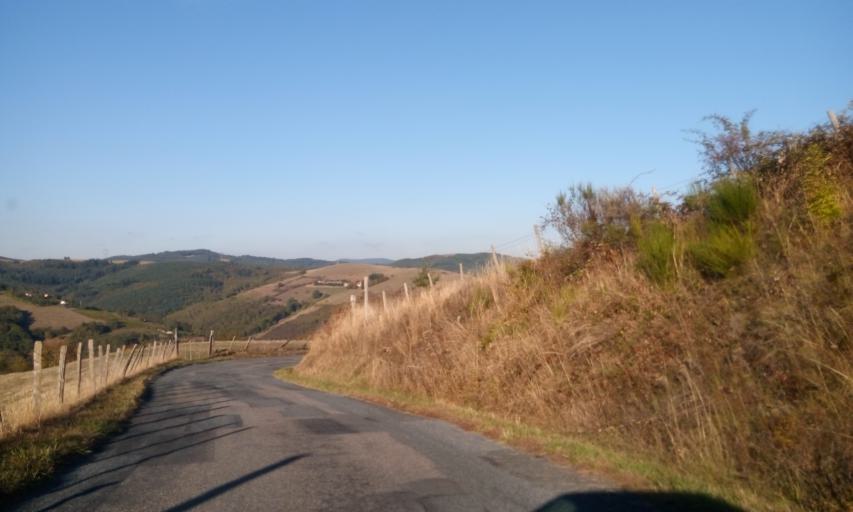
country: FR
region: Rhone-Alpes
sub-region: Departement du Rhone
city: Tarare
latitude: 45.9163
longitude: 4.4504
